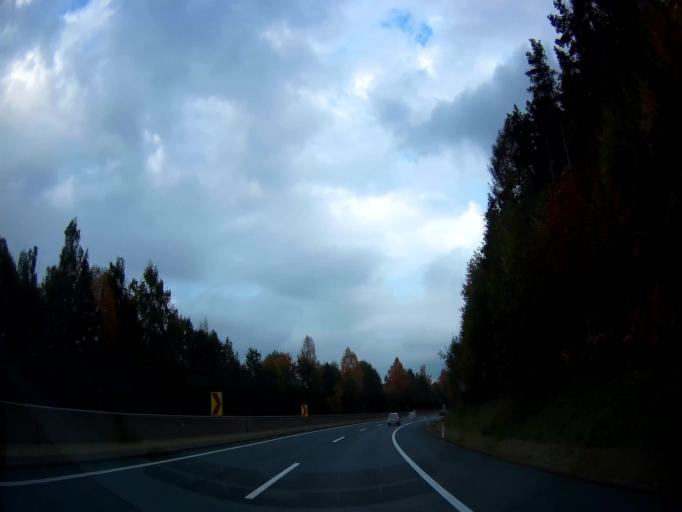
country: AT
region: Styria
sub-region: Politischer Bezirk Voitsberg
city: Ligist
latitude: 46.9747
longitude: 15.1962
